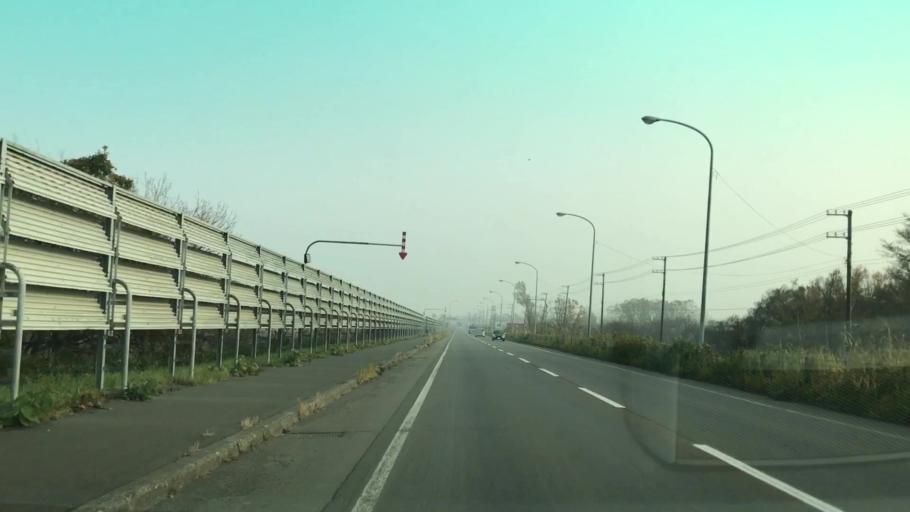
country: JP
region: Hokkaido
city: Ishikari
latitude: 43.2385
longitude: 141.3640
